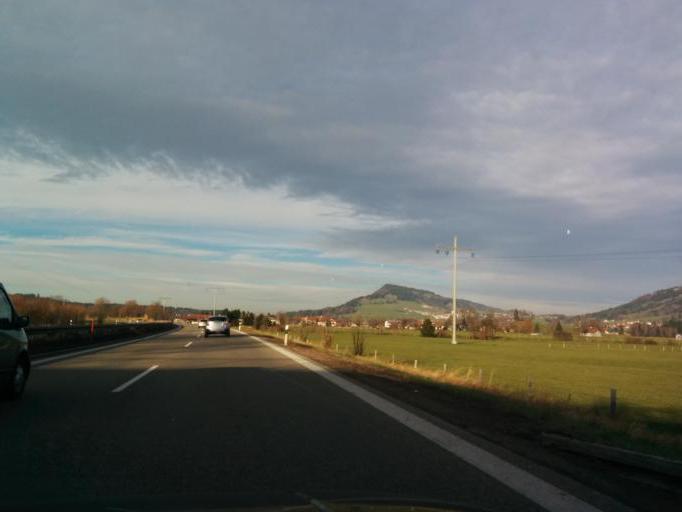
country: DE
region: Bavaria
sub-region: Swabia
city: Blaichach
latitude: 47.5407
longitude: 10.2677
